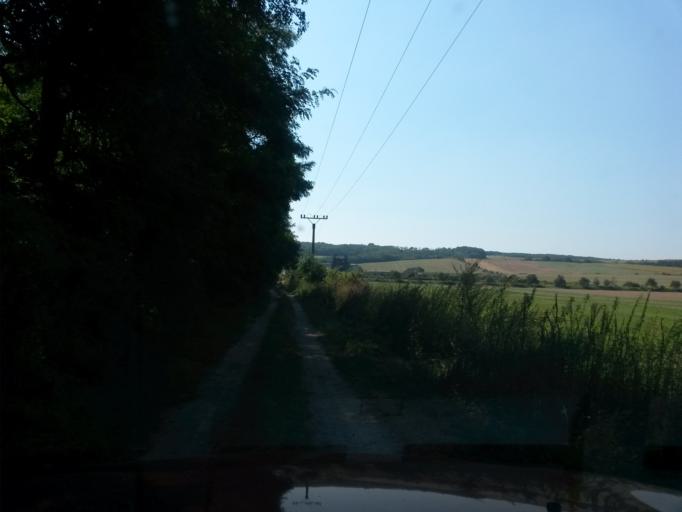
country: HU
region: Borsod-Abauj-Zemplen
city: Gonc
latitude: 48.5366
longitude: 21.1565
